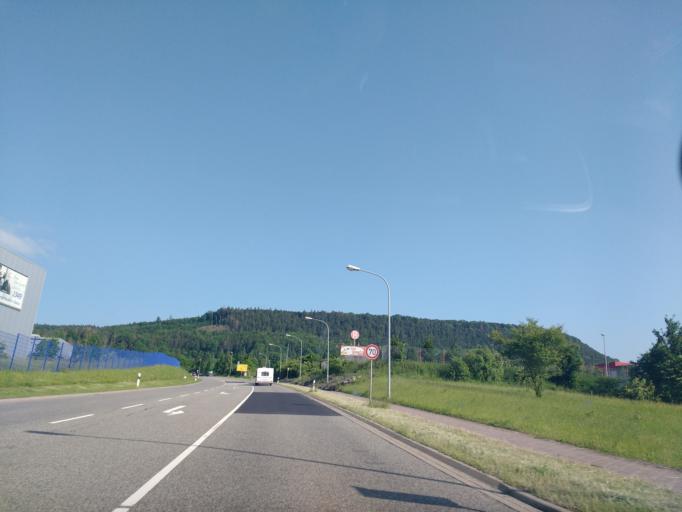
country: DE
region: Thuringia
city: Heilbad Heiligenstadt
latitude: 51.3846
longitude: 10.1552
